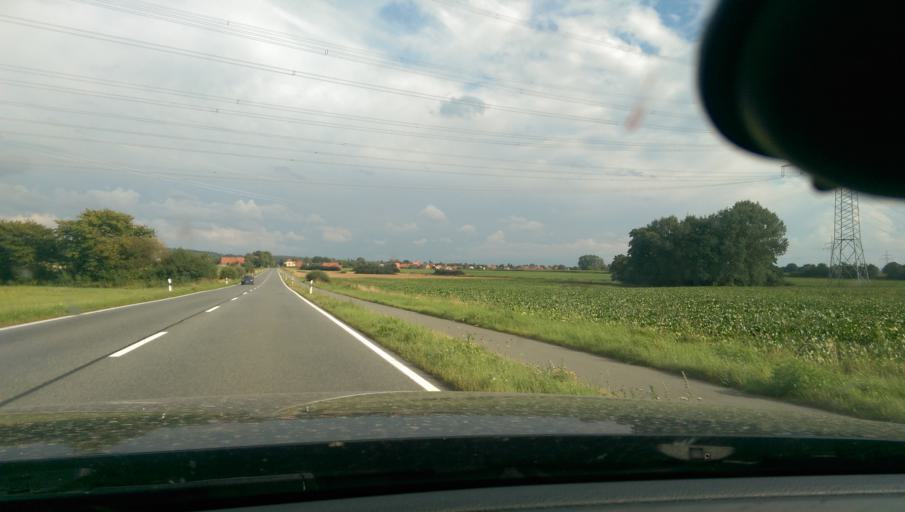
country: DE
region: Lower Saxony
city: Rehburg-Loccum
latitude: 52.4477
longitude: 9.1712
